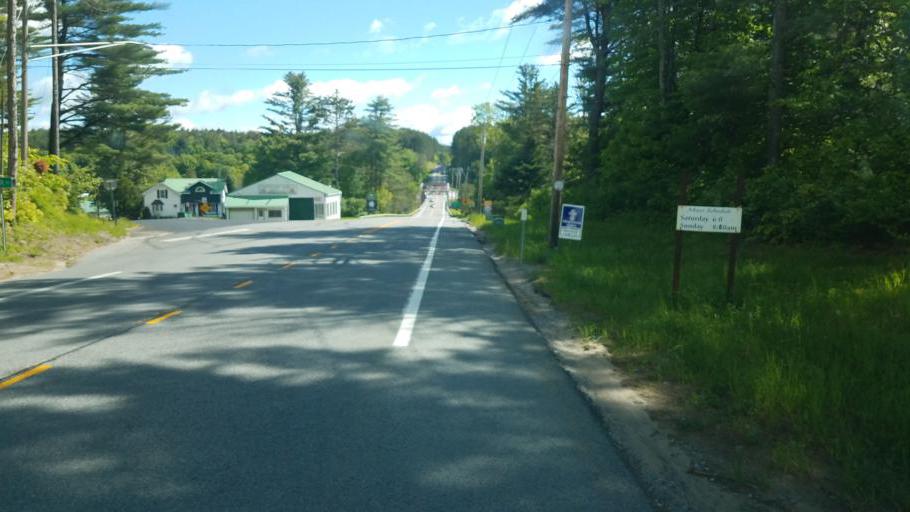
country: US
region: New York
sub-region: Oneida County
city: Boonville
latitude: 43.4371
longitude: -75.2065
